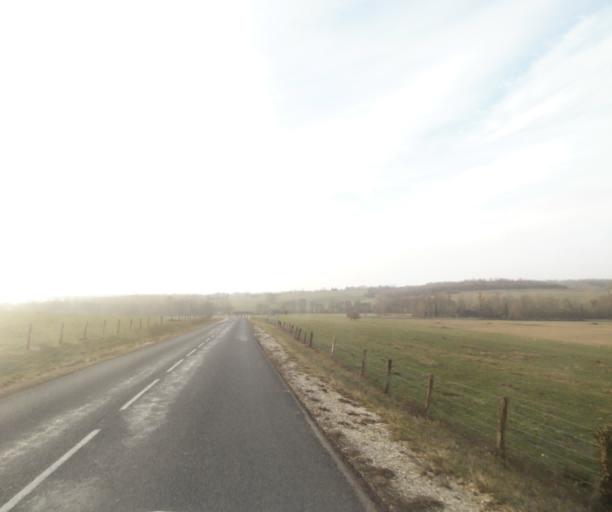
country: FR
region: Champagne-Ardenne
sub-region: Departement de la Marne
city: Sermaize-les-Bains
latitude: 48.7486
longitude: 4.9043
